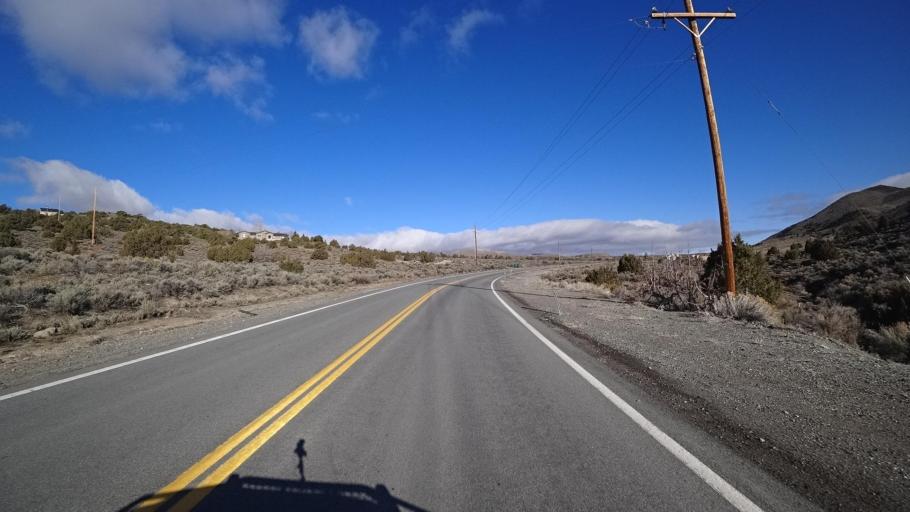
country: US
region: Nevada
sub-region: Washoe County
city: Lemmon Valley
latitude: 39.7353
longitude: -119.8829
